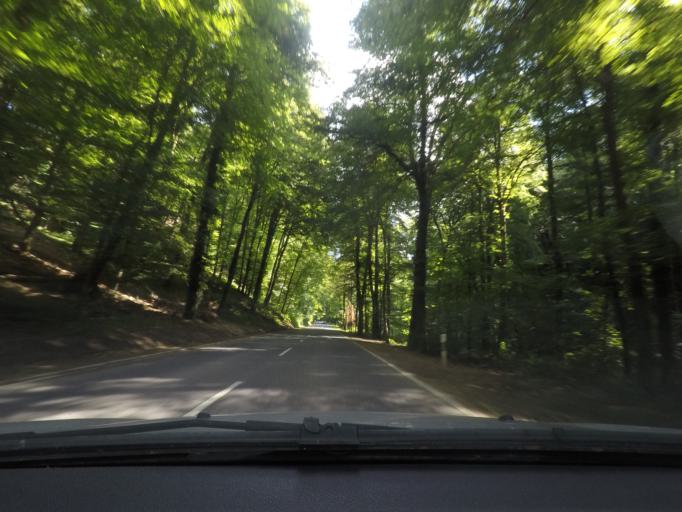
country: LU
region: Grevenmacher
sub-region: Canton d'Echternach
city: Waldbillig
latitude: 49.7783
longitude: 6.2937
